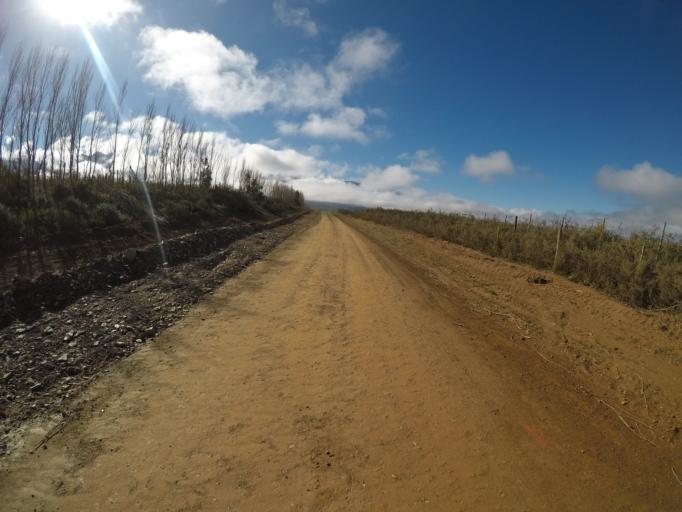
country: ZA
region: Western Cape
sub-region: Overberg District Municipality
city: Caledon
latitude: -34.1180
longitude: 19.7371
